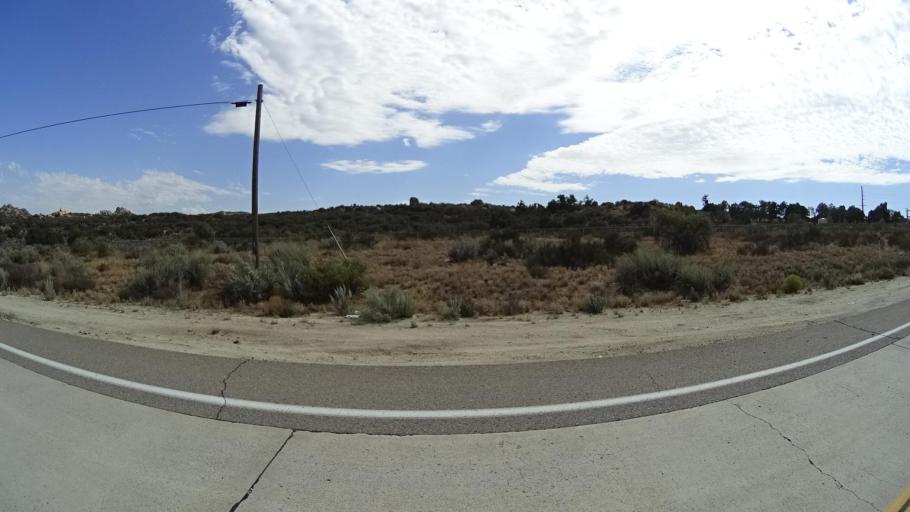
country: MX
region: Baja California
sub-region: Tecate
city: Cereso del Hongo
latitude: 32.6627
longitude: -116.2701
